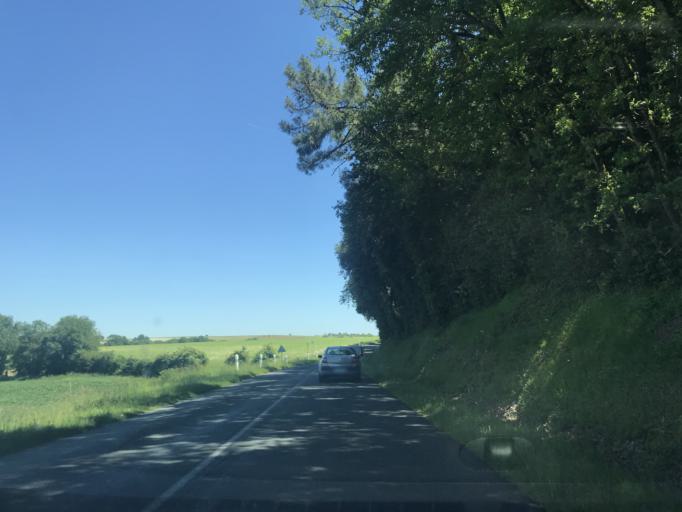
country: FR
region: Poitou-Charentes
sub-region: Departement de la Charente-Maritime
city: Meschers-sur-Gironde
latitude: 45.5926
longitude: -0.9672
